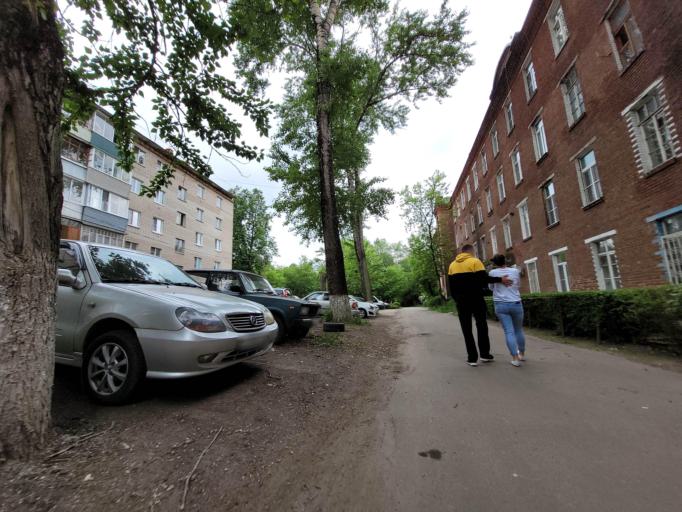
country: RU
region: Moskovskaya
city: Lesnyye Polyany
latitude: 55.9446
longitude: 37.8656
